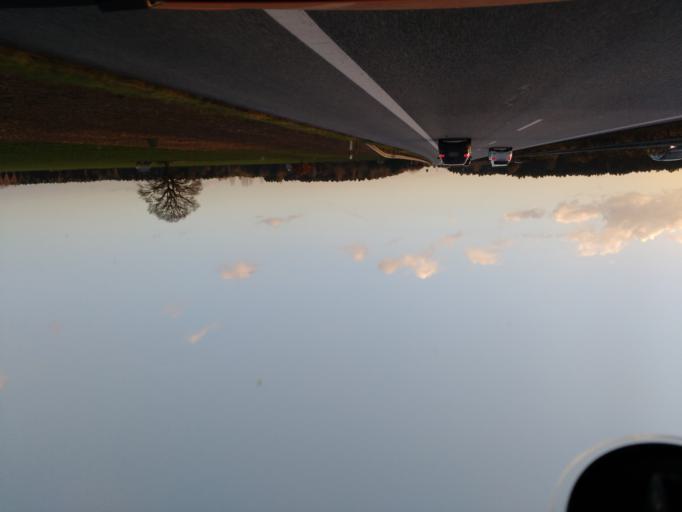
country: DE
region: Mecklenburg-Vorpommern
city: Sulstorf
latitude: 53.4751
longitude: 11.3029
